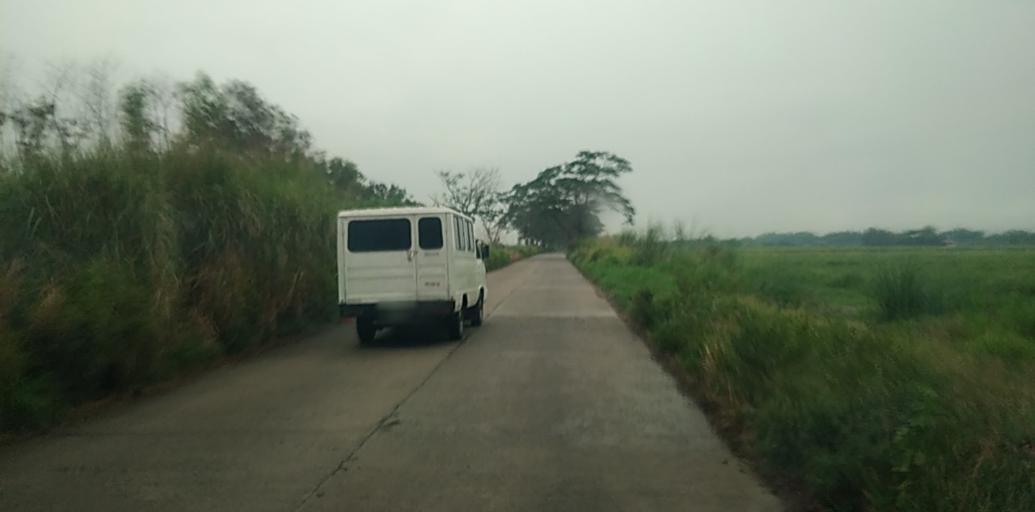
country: PH
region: Central Luzon
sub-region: Province of Pampanga
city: San Antonio
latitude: 15.1536
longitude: 120.6983
